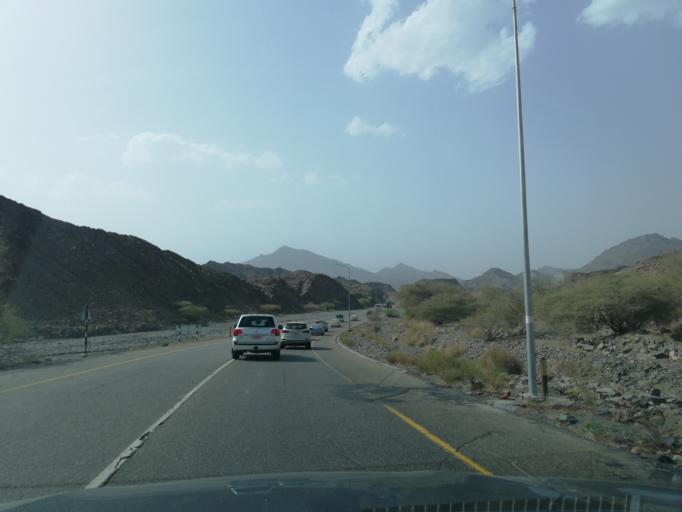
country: OM
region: Muhafazat ad Dakhiliyah
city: Sufalat Sama'il
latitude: 23.2002
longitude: 58.0828
